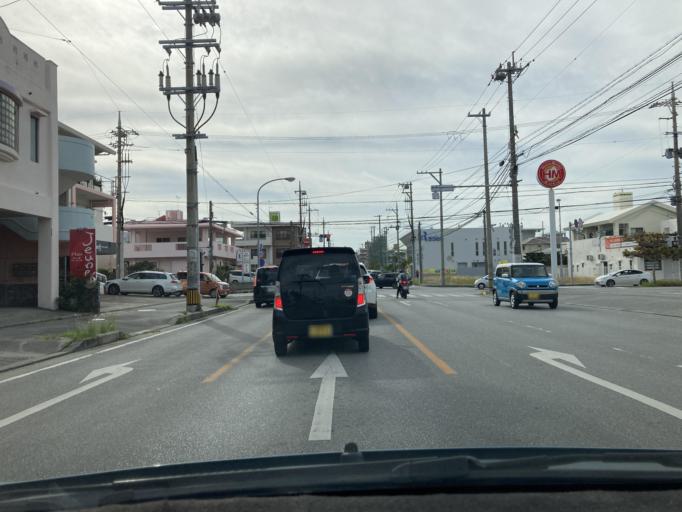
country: JP
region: Okinawa
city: Okinawa
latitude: 26.3442
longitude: 127.8274
